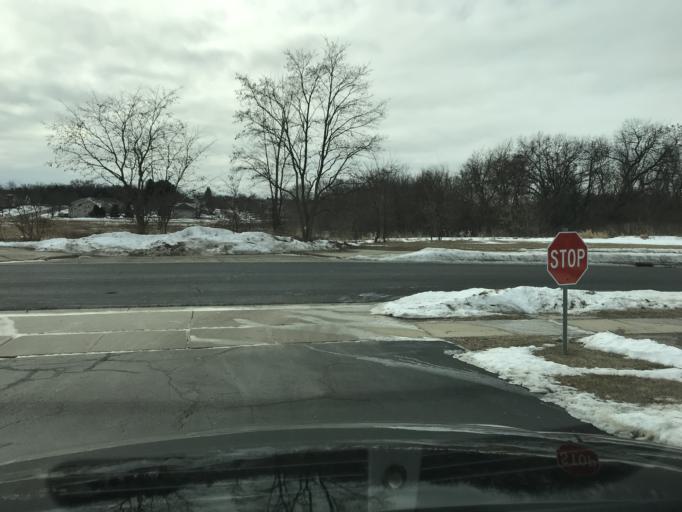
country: US
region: Wisconsin
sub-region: Dane County
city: Cottage Grove
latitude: 43.0911
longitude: -89.2634
